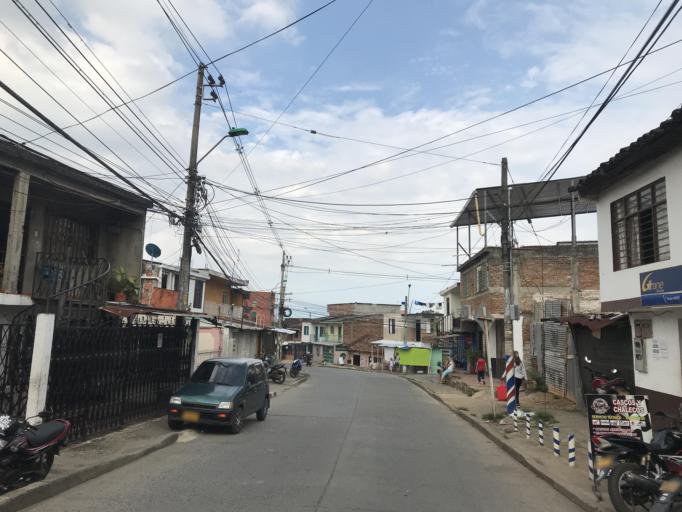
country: CO
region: Valle del Cauca
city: Cali
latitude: 3.3742
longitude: -76.5534
